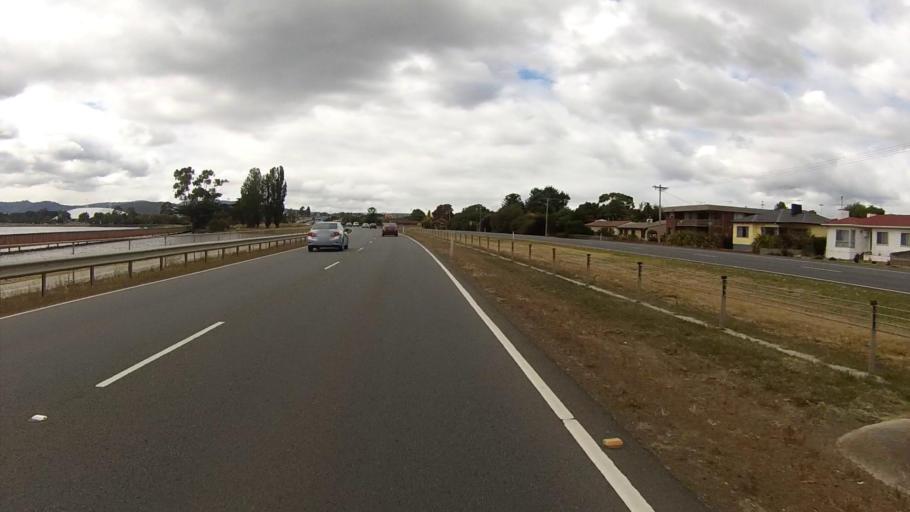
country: AU
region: Tasmania
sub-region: Glenorchy
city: Glenorchy
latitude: -42.8251
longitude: 147.2735
